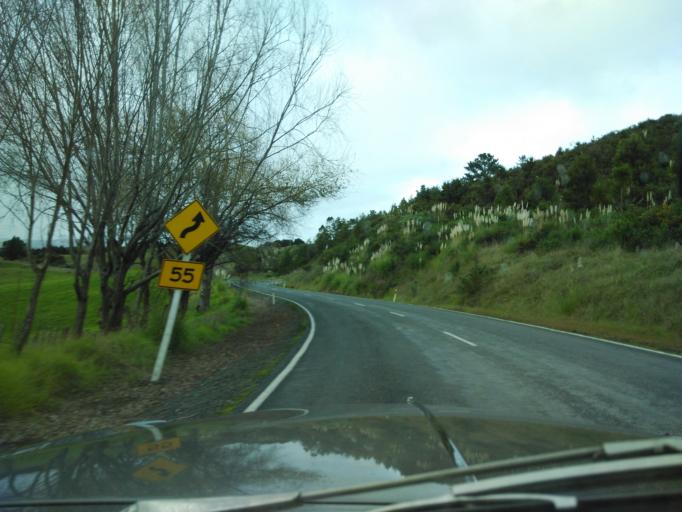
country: NZ
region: Auckland
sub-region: Auckland
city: Wellsford
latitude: -36.3329
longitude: 174.3816
